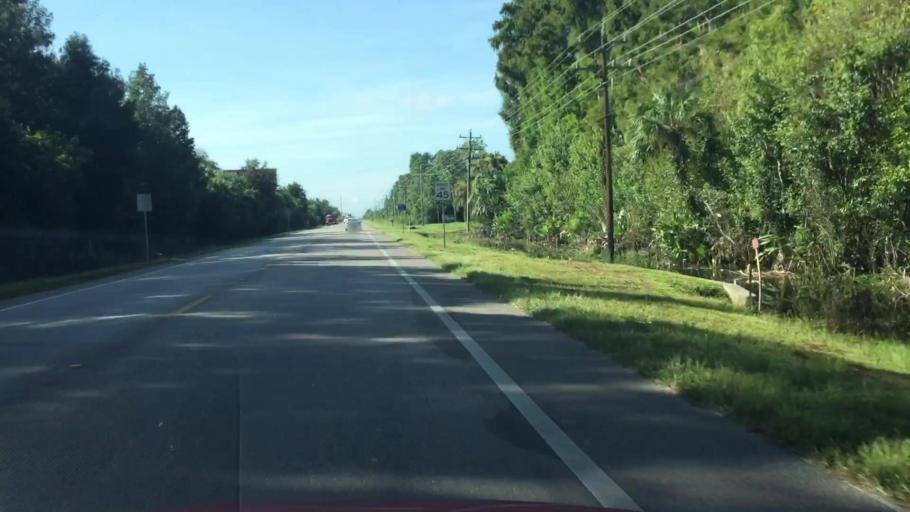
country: US
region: Florida
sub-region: Collier County
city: Immokalee
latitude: 26.4049
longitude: -81.4172
